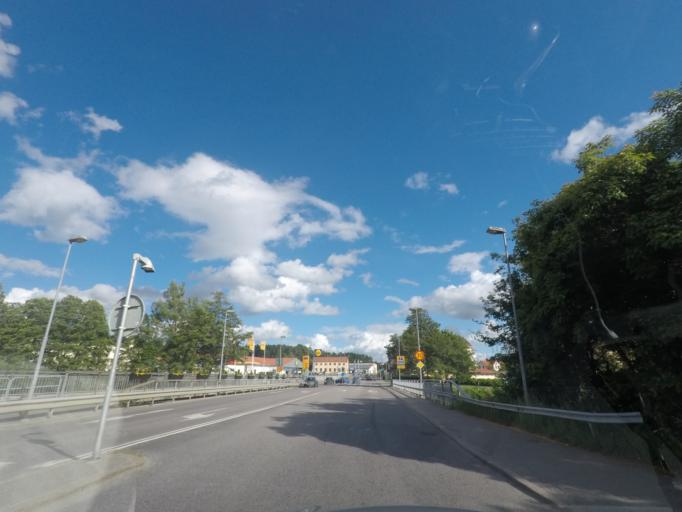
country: SE
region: OErebro
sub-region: Lindesbergs Kommun
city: Lindesberg
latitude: 59.5987
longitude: 15.2222
